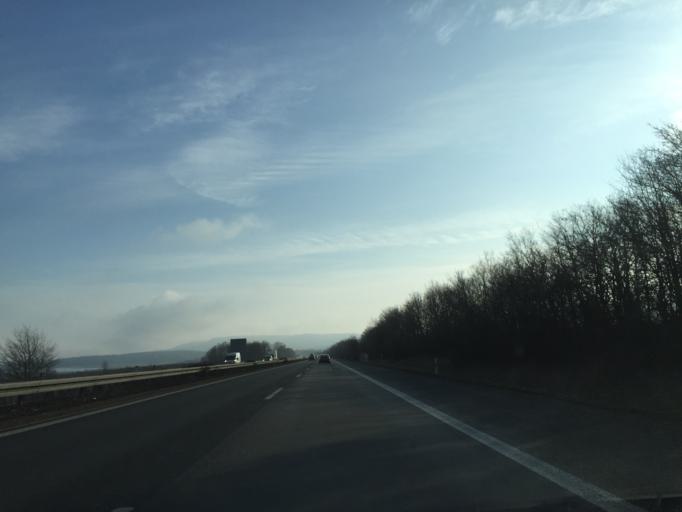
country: DE
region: Bavaria
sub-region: Regierungsbezirk Unterfranken
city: Wiesentheid
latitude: 49.7745
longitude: 10.3589
